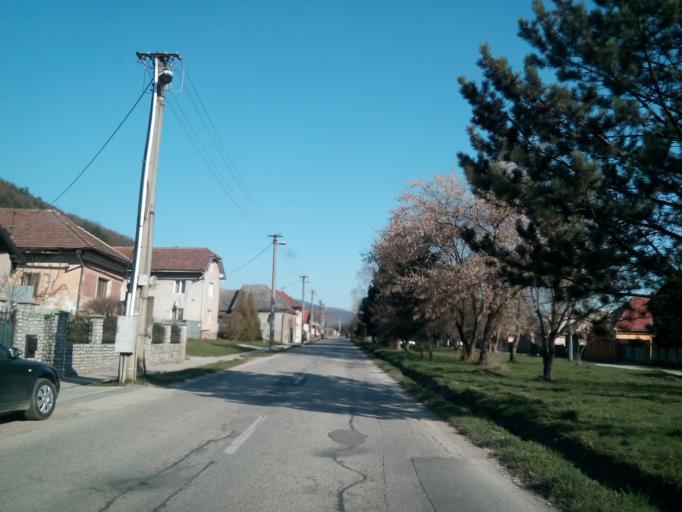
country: SK
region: Kosicky
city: Dobsina
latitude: 48.6613
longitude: 20.3627
